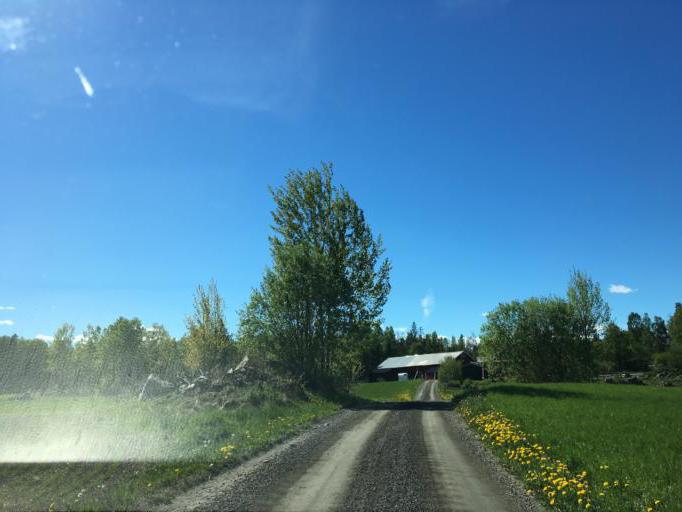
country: SE
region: Soedermanland
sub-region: Eskilstuna Kommun
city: Hallbybrunn
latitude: 59.3514
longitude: 16.3320
